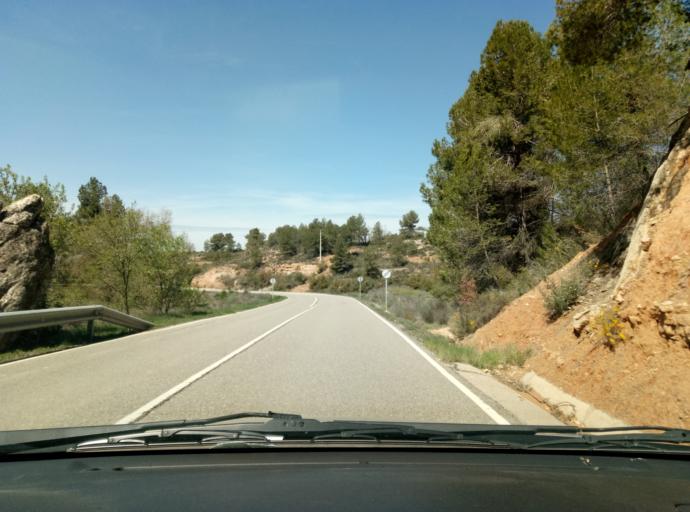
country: ES
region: Catalonia
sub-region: Provincia de Tarragona
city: Ulldemolins
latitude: 41.4257
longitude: 0.8760
